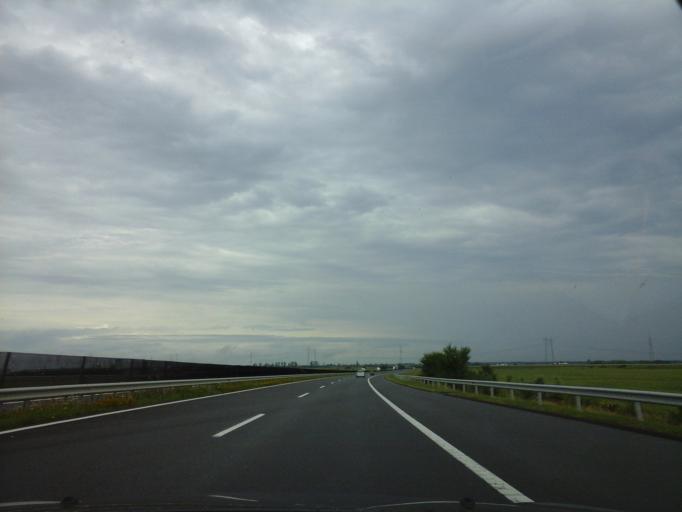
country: HU
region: Hajdu-Bihar
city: Polgar
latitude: 47.8252
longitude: 21.1509
